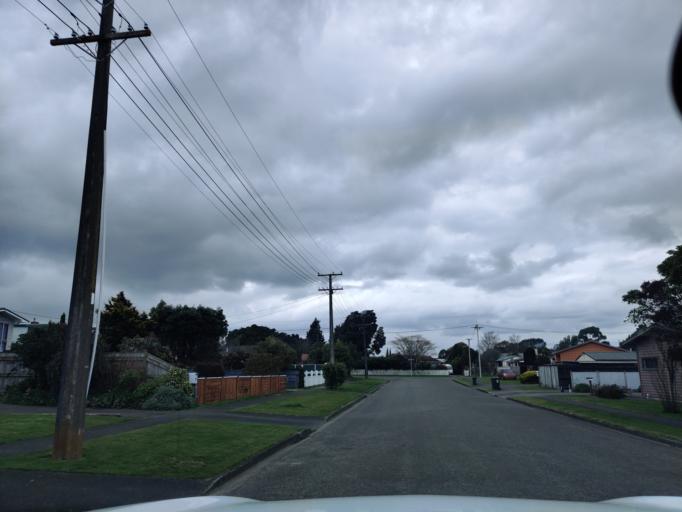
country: NZ
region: Manawatu-Wanganui
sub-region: Palmerston North City
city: Palmerston North
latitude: -40.2904
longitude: 175.7598
